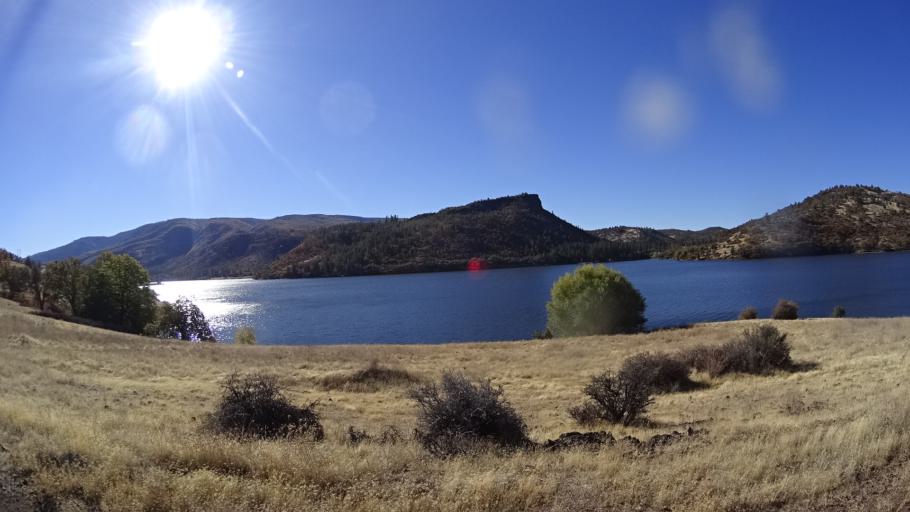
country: US
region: California
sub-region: Siskiyou County
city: Montague
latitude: 41.9823
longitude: -122.2963
